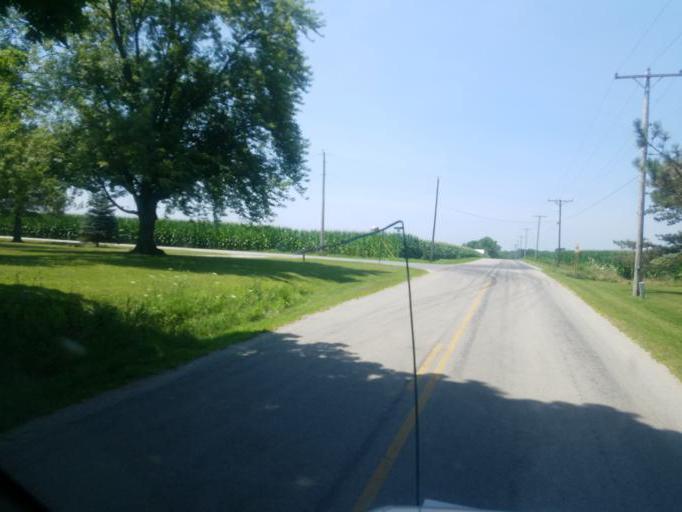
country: US
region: Ohio
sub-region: Shelby County
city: Sidney
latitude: 40.3061
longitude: -84.1076
